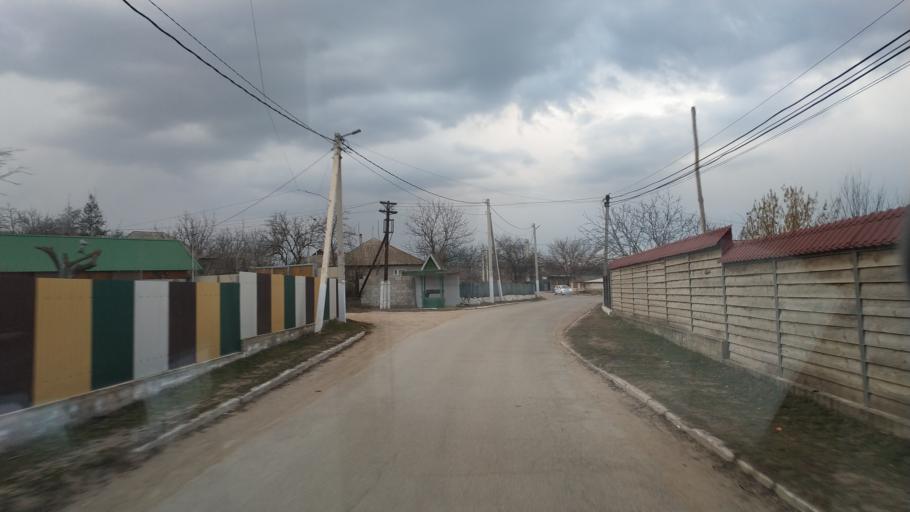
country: MD
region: Telenesti
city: Grigoriopol
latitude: 47.0221
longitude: 29.3581
